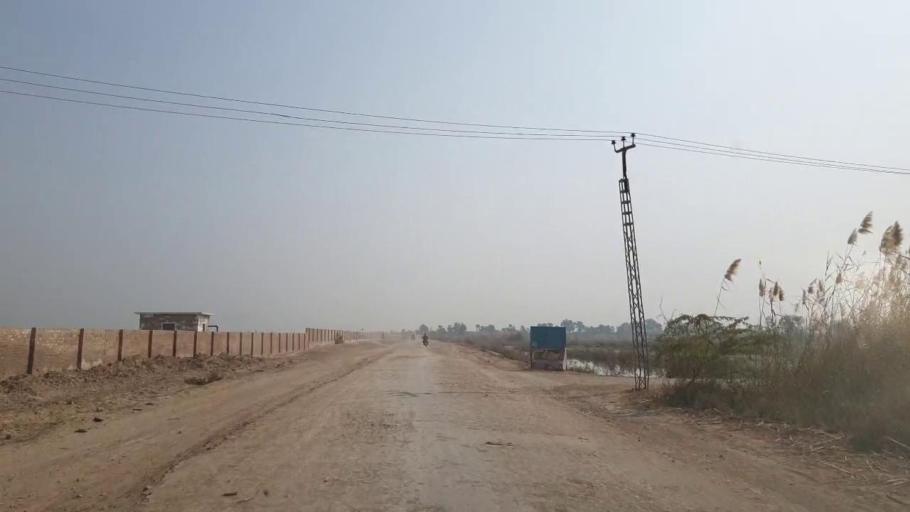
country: PK
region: Sindh
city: Mirpur Khas
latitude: 25.5556
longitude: 69.0900
